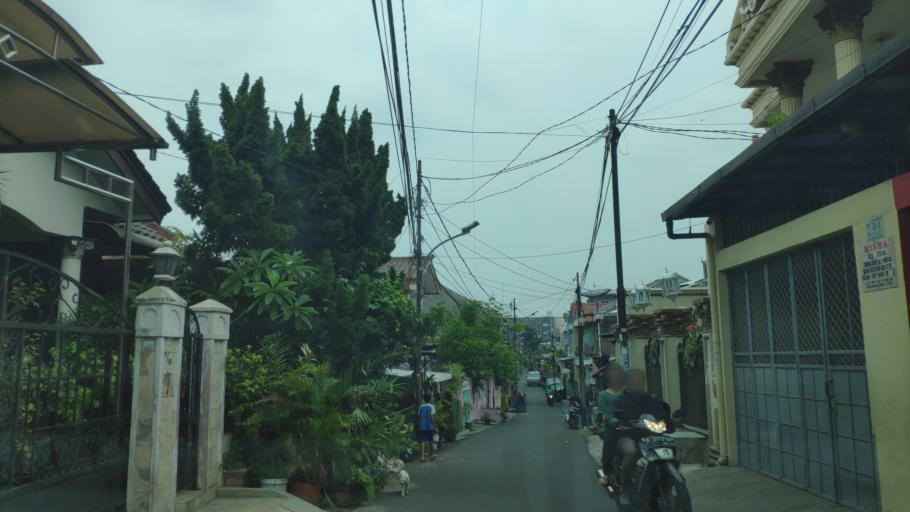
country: ID
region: Jakarta Raya
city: Jakarta
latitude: -6.1930
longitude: 106.7990
